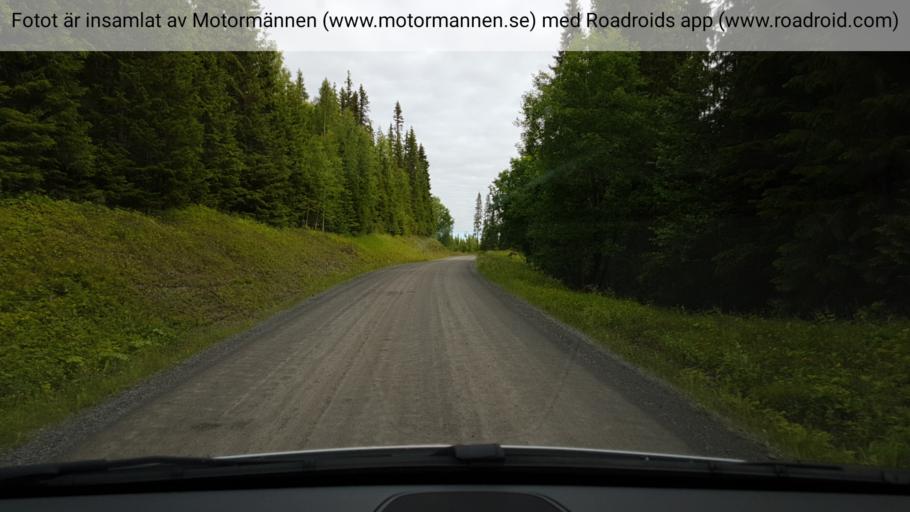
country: SE
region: Jaemtland
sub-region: OEstersunds Kommun
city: Lit
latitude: 63.4338
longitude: 15.2655
